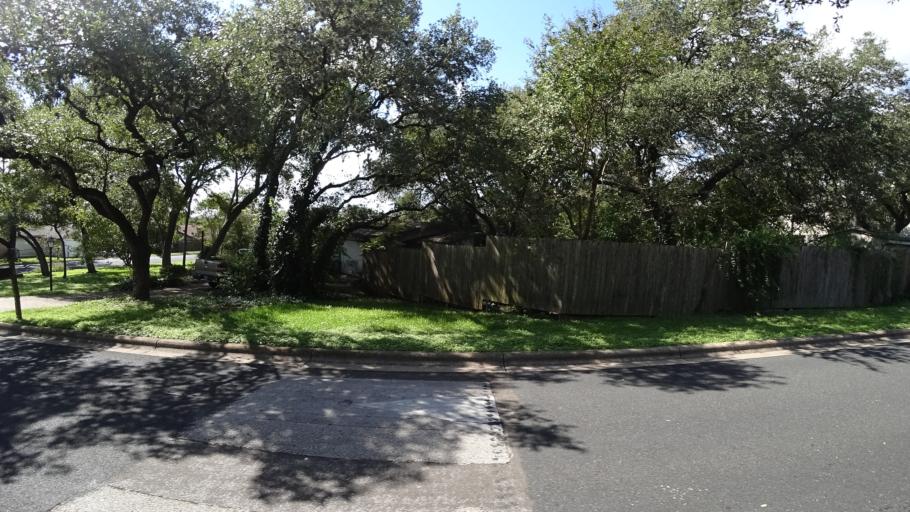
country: US
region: Texas
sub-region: Travis County
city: Shady Hollow
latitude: 30.2015
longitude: -97.8106
